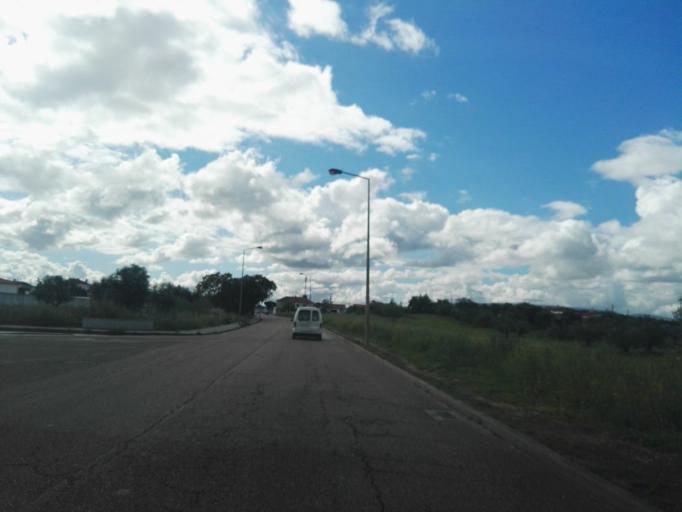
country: PT
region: Santarem
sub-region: Torres Novas
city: Riachos
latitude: 39.4475
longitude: -8.5092
